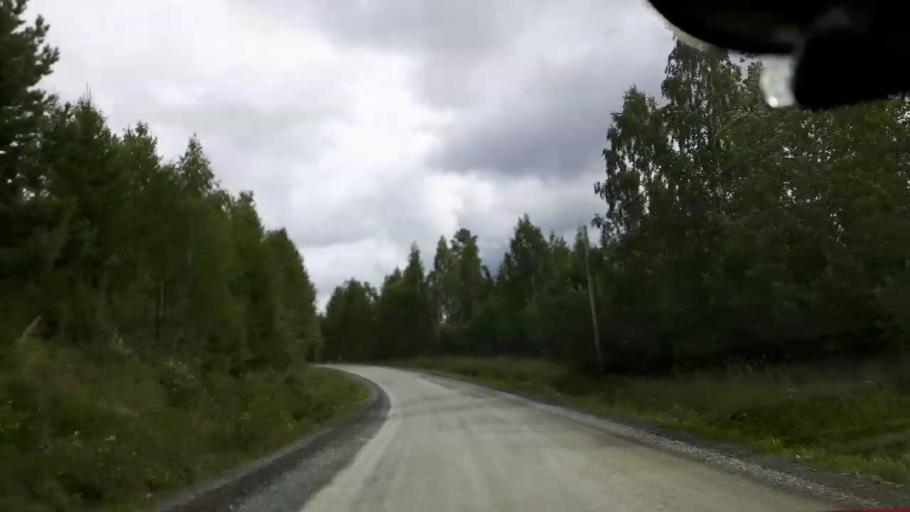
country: SE
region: Jaemtland
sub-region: Krokoms Kommun
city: Valla
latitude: 63.5828
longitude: 14.1726
